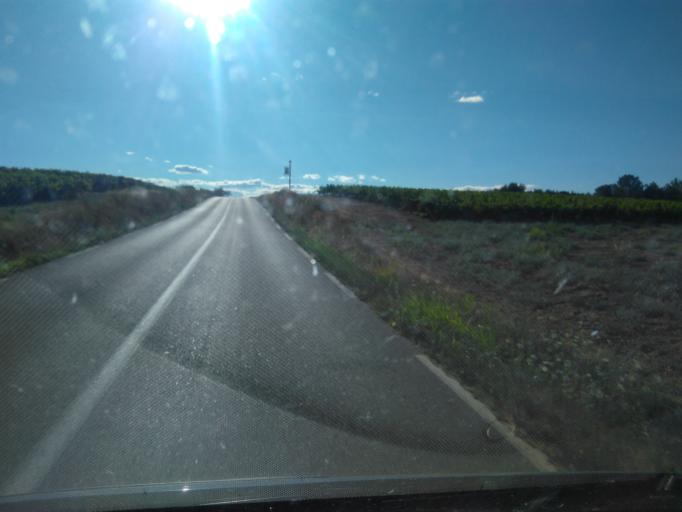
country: FR
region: Languedoc-Roussillon
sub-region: Departement du Gard
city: Vauvert
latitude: 43.6524
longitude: 4.3063
